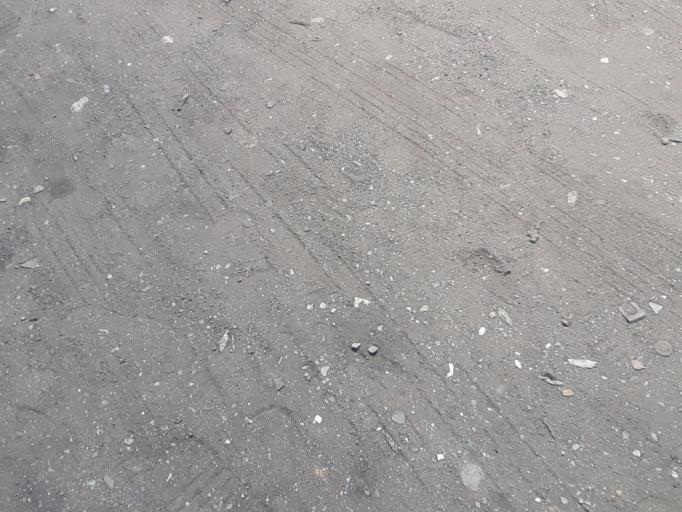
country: ZM
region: Lusaka
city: Lusaka
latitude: -15.3665
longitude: 28.2921
